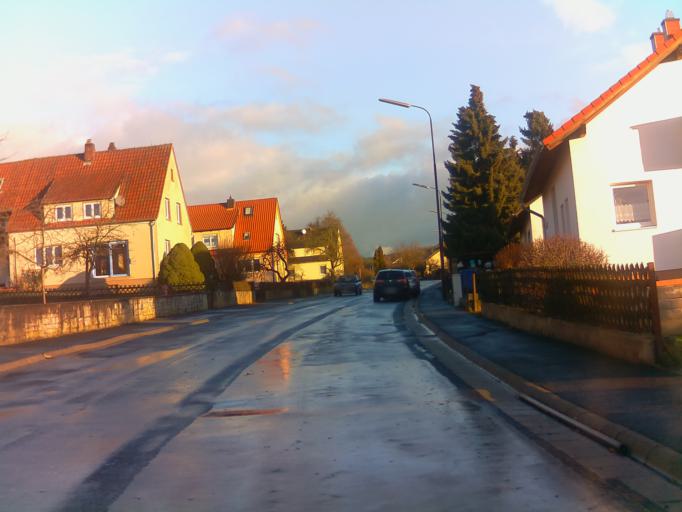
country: DE
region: Bavaria
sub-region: Regierungsbezirk Unterfranken
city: Sondheim vor der Rhoen
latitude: 50.4795
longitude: 10.1866
